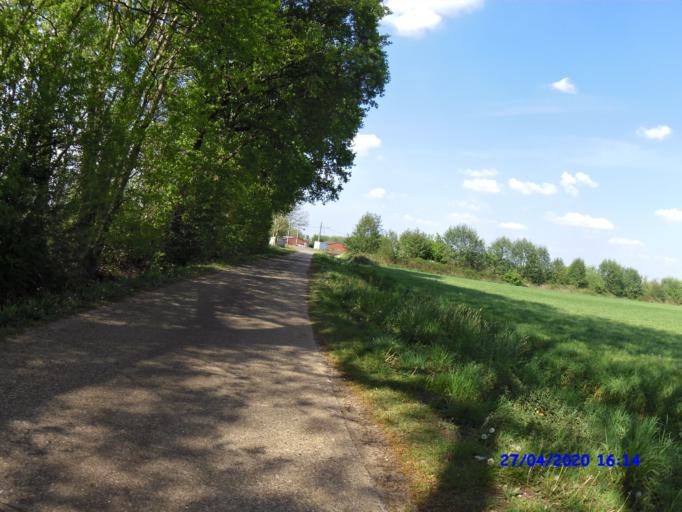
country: BE
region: Flanders
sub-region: Provincie Antwerpen
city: Lille
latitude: 51.2250
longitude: 4.8778
